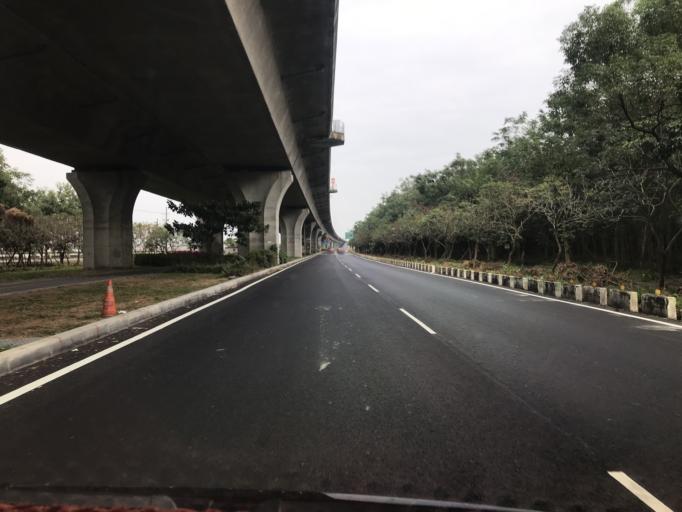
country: TW
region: Taiwan
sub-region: Pingtung
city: Pingtung
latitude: 22.6418
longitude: 120.5397
